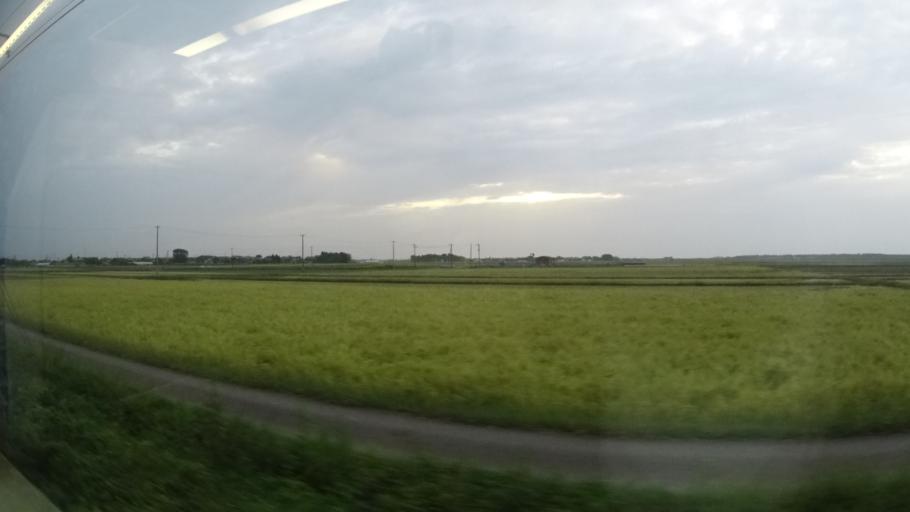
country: JP
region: Niigata
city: Murakami
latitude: 38.1542
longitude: 139.4591
